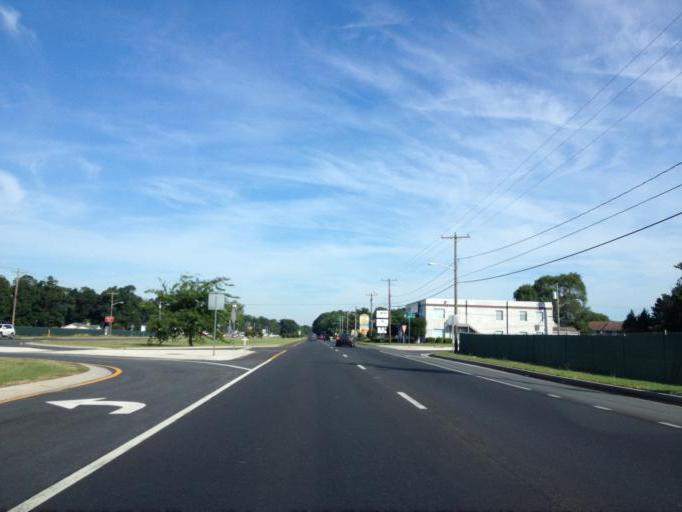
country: US
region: Delaware
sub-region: Sussex County
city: Millsboro
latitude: 38.5898
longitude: -75.3022
